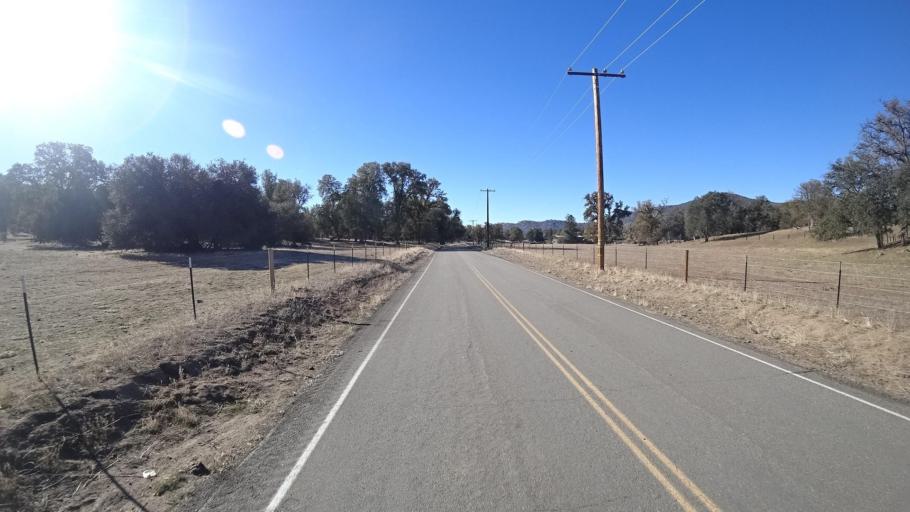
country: US
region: California
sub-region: Kern County
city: Alta Sierra
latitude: 35.7739
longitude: -118.7072
